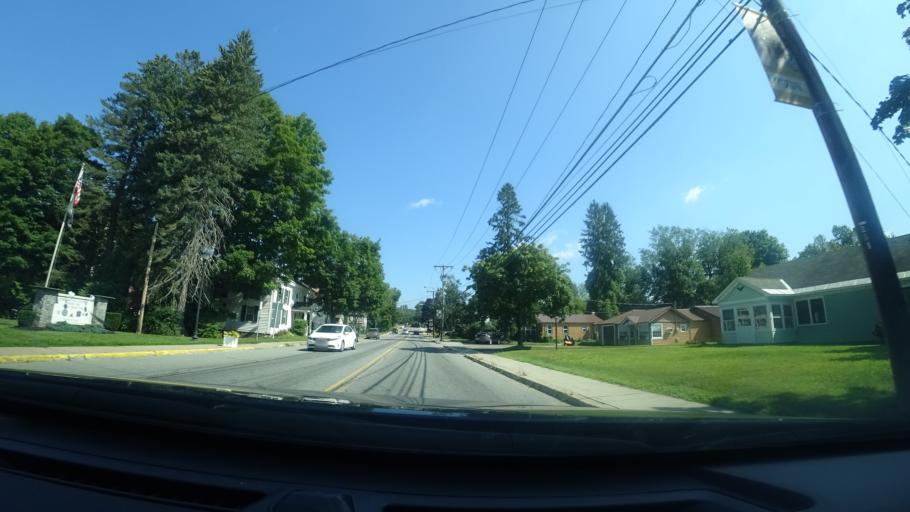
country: US
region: New York
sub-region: Warren County
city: Warrensburg
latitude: 43.6499
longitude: -73.8010
